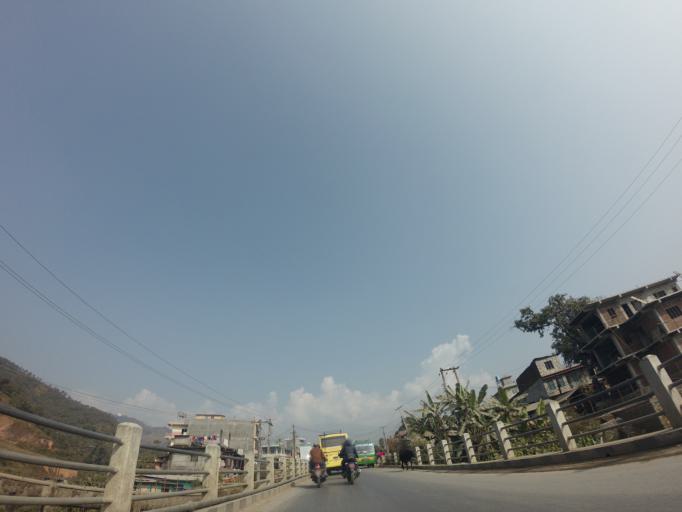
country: NP
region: Western Region
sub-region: Gandaki Zone
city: Pokhara
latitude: 28.2284
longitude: 83.9813
